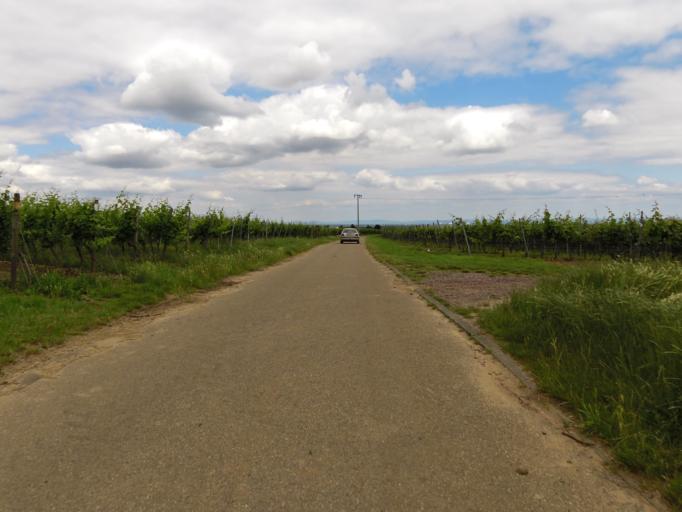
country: DE
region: Rheinland-Pfalz
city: Kallstadt
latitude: 49.4839
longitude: 8.1703
